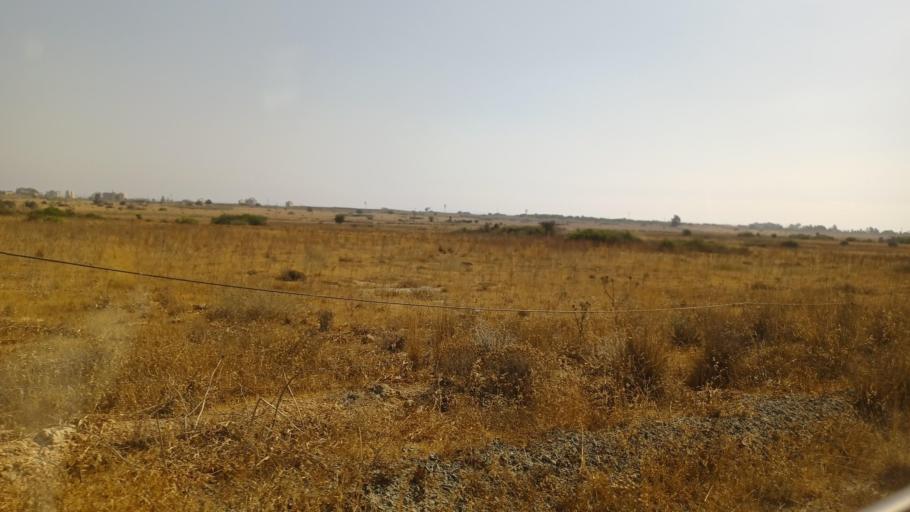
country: CY
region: Ammochostos
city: Deryneia
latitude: 35.0702
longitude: 33.9685
